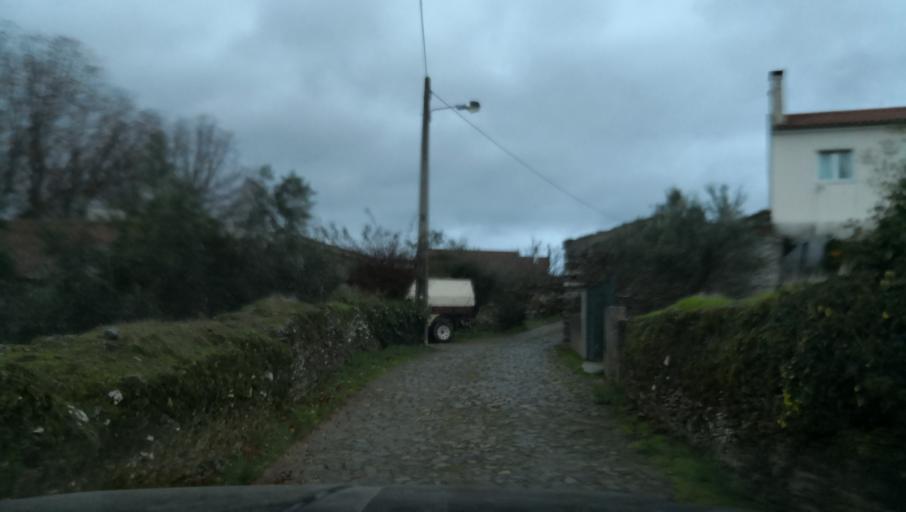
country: PT
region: Vila Real
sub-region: Vila Real
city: Vila Real
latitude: 41.2538
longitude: -7.7365
